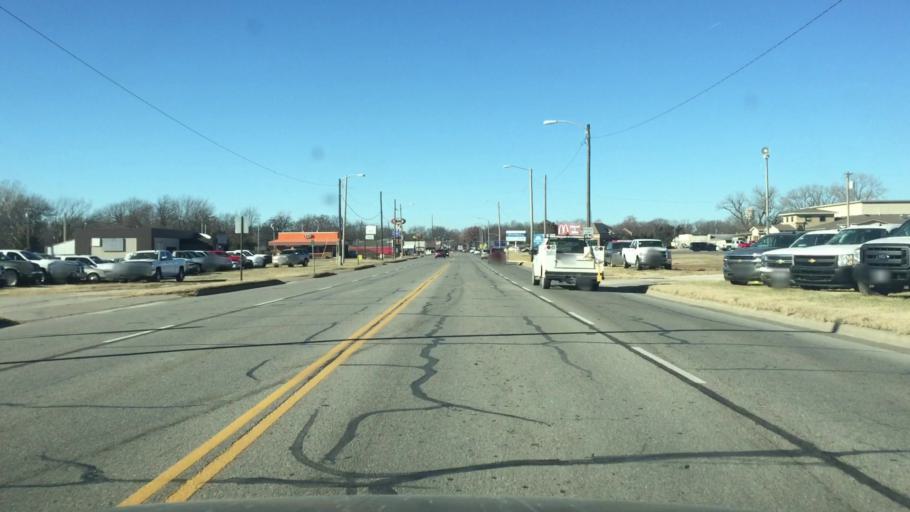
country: US
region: Kansas
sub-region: Allen County
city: Iola
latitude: 37.9221
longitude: -95.3856
